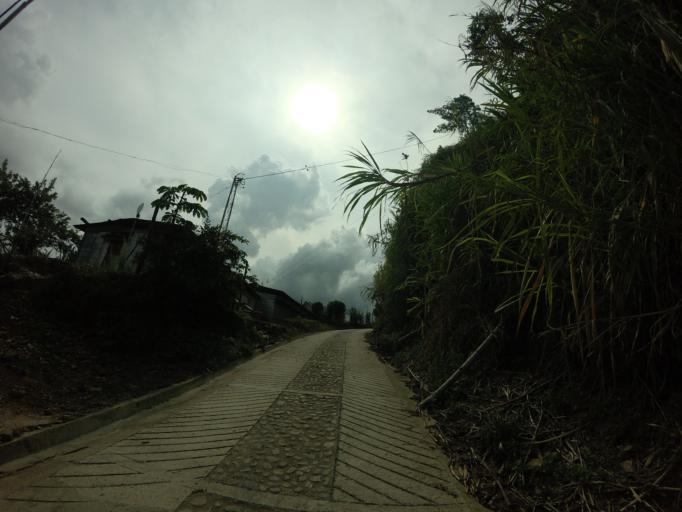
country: CO
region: Caldas
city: Marquetalia
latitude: 5.3366
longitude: -75.0460
